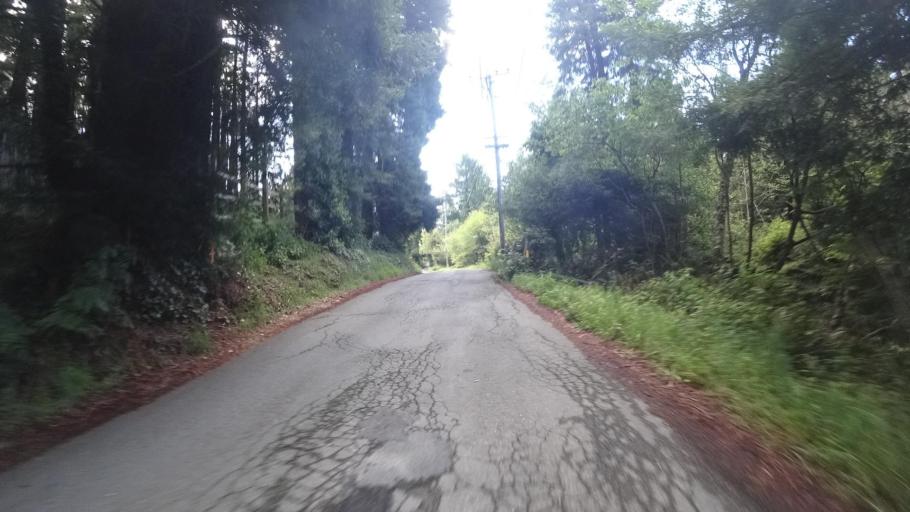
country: US
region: California
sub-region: Humboldt County
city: Westhaven-Moonstone
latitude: 41.0481
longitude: -124.1196
